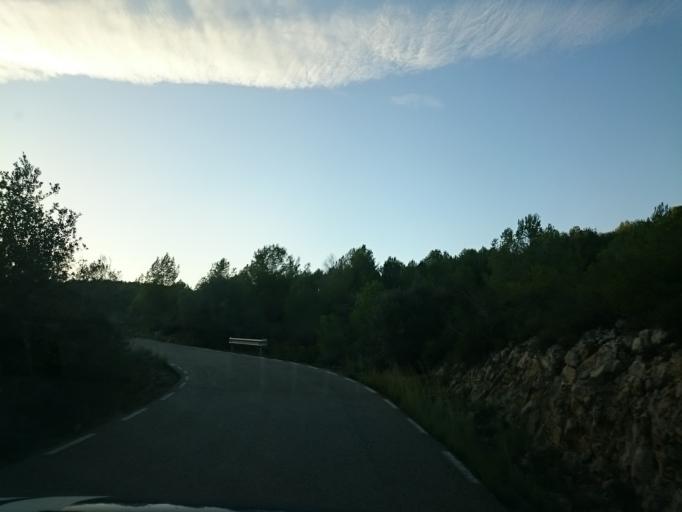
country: ES
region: Catalonia
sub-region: Provincia de Barcelona
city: Olivella
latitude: 41.3064
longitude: 1.8205
